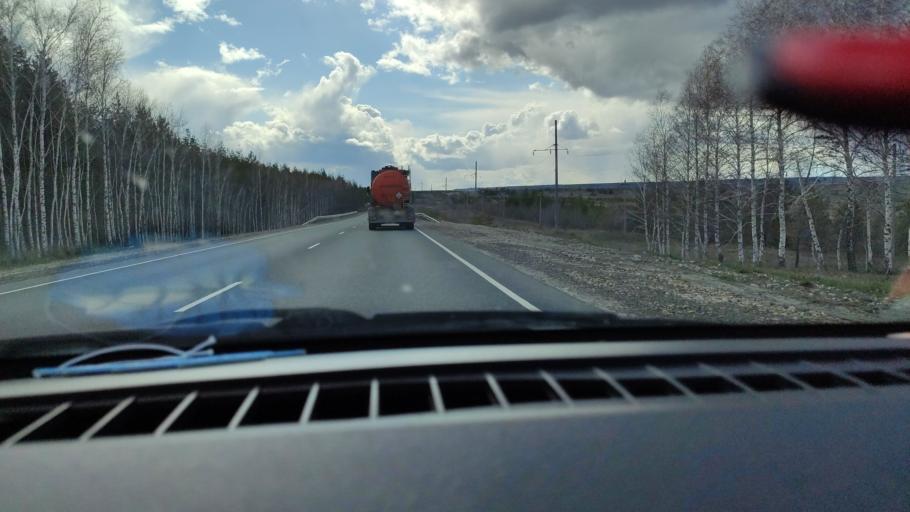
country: RU
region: Saratov
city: Khvalynsk
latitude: 52.5384
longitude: 48.0487
